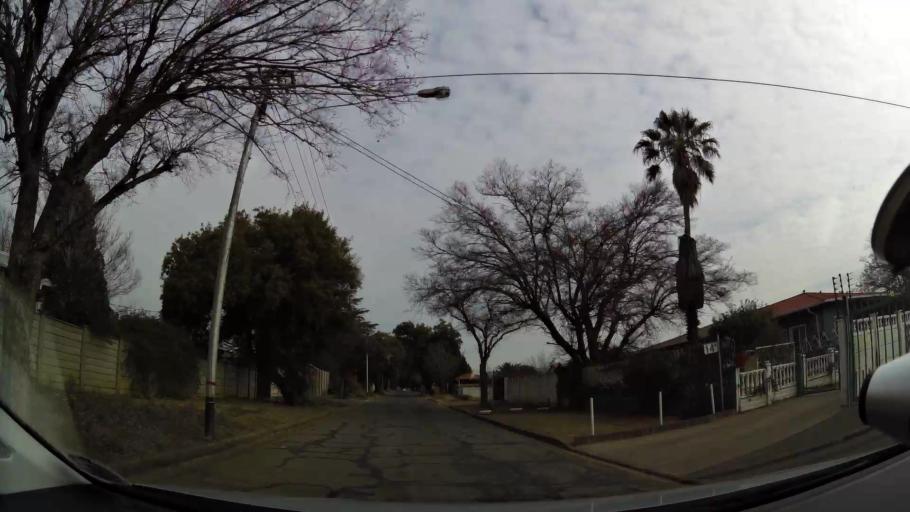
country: ZA
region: Orange Free State
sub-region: Mangaung Metropolitan Municipality
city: Bloemfontein
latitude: -29.1268
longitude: 26.1933
